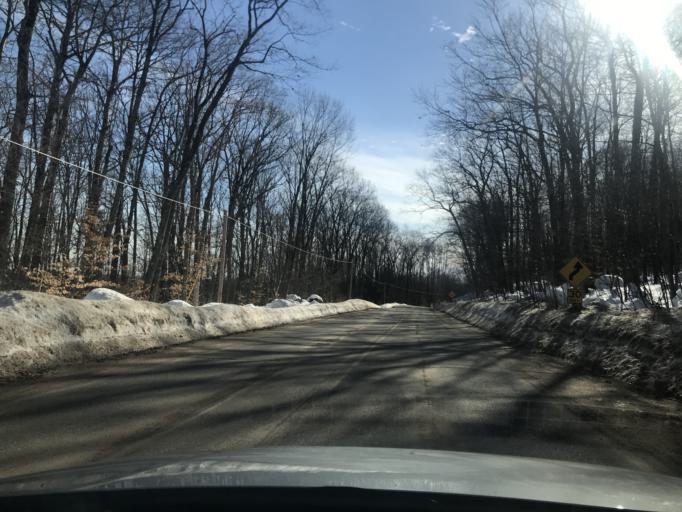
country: US
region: Michigan
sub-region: Dickinson County
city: Kingsford
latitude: 45.4063
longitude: -88.3483
